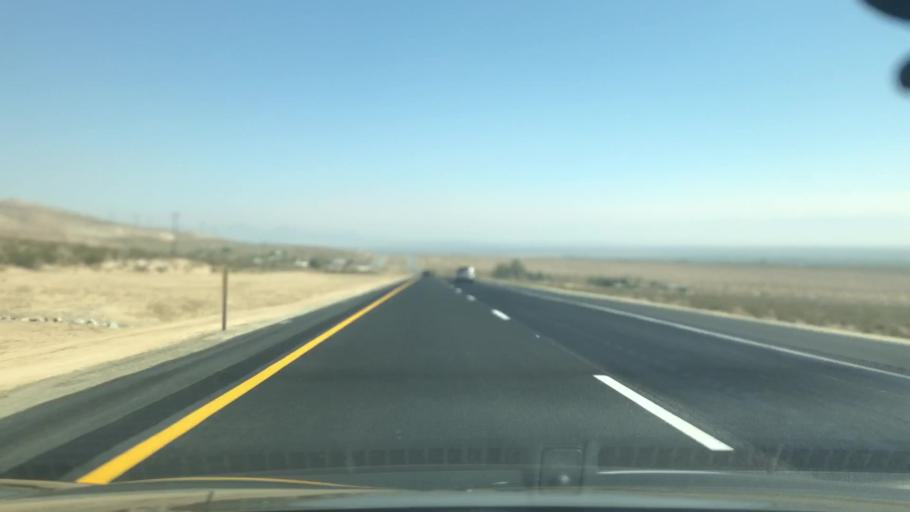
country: US
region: California
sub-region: Kern County
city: Inyokern
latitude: 35.6587
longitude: -117.8750
